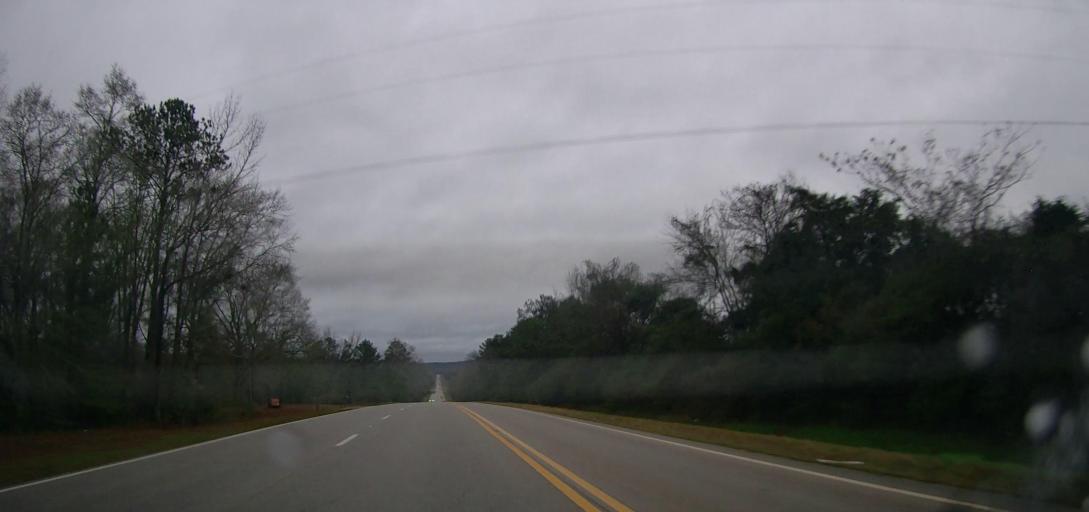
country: US
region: Alabama
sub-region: Bibb County
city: Centreville
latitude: 32.8555
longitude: -86.9648
